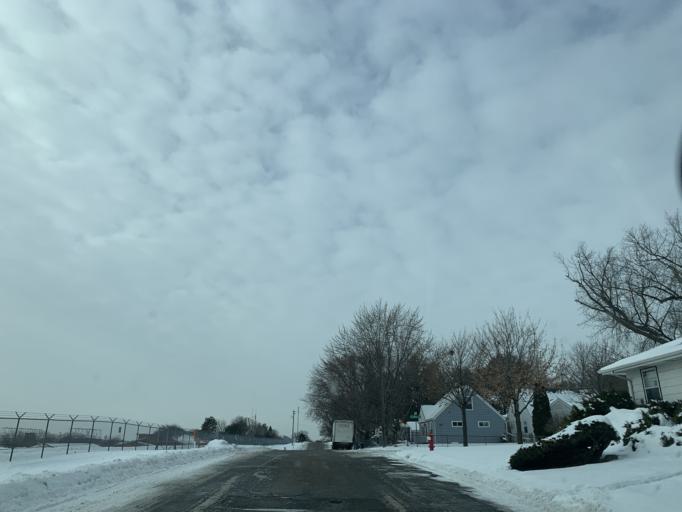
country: US
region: Minnesota
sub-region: Dakota County
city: Mendota Heights
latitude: 44.8964
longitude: -93.2084
